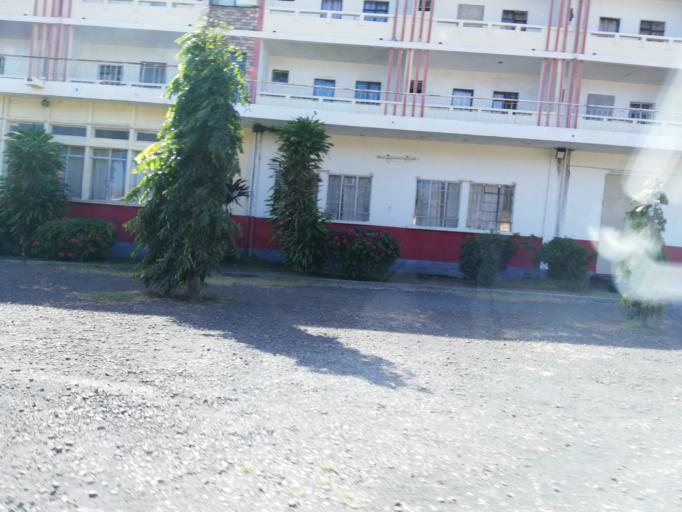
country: MU
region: Moka
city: Pailles
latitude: -20.1864
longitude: 57.4717
